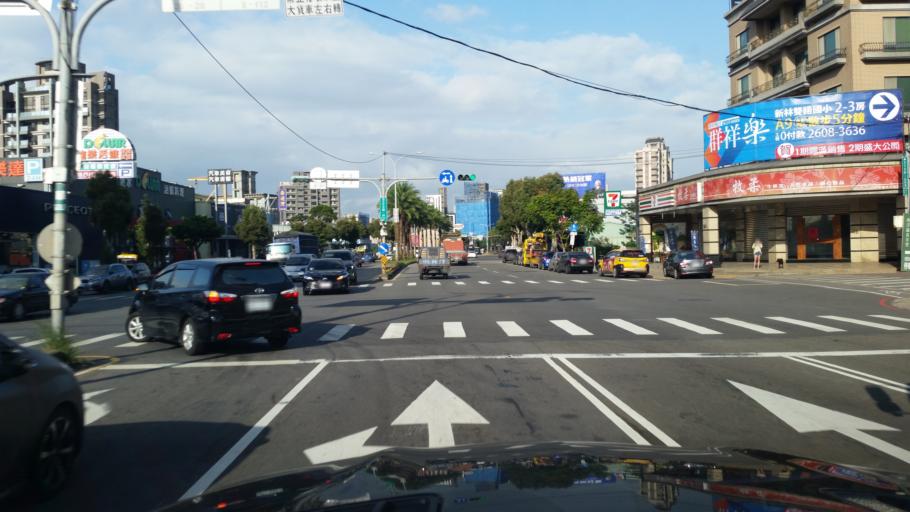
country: TW
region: Taiwan
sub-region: Taoyuan
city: Taoyuan
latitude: 25.0686
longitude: 121.3563
